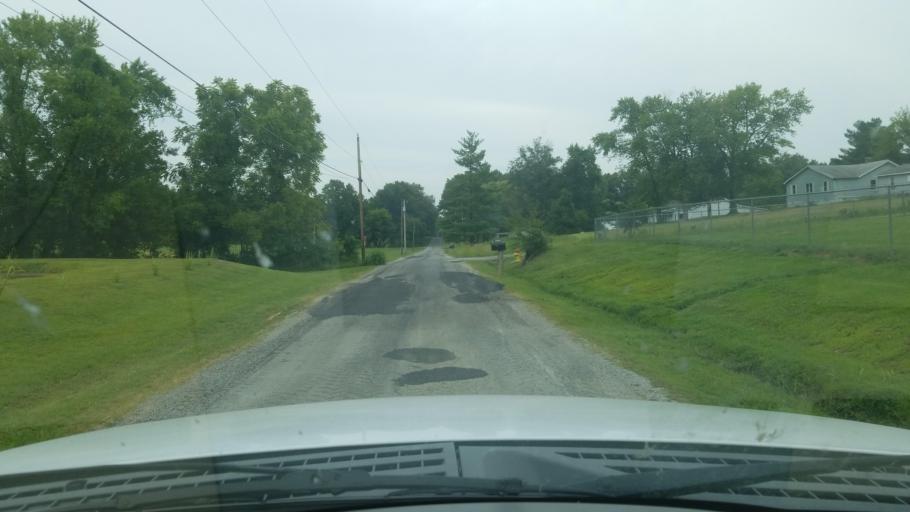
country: US
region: Illinois
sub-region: Saline County
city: Eldorado
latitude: 37.8229
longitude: -88.4477
